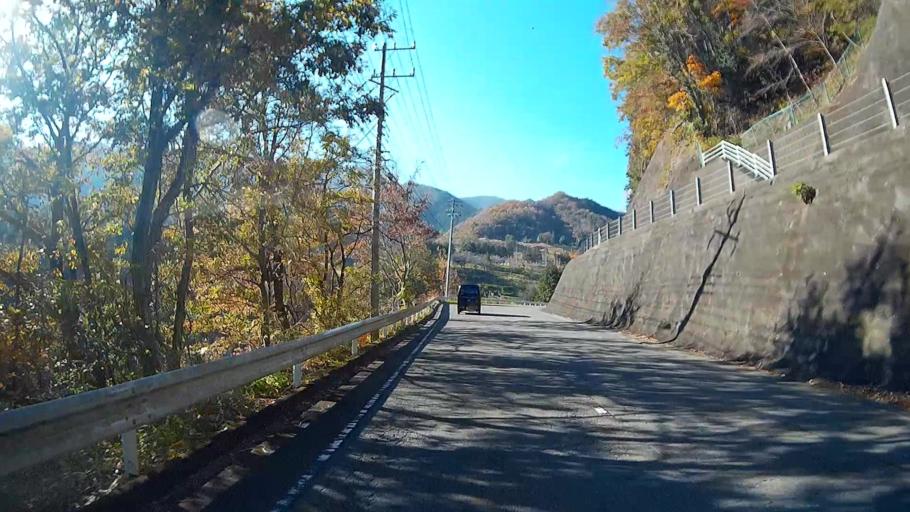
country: JP
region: Yamanashi
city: Uenohara
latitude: 35.5683
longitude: 139.0889
